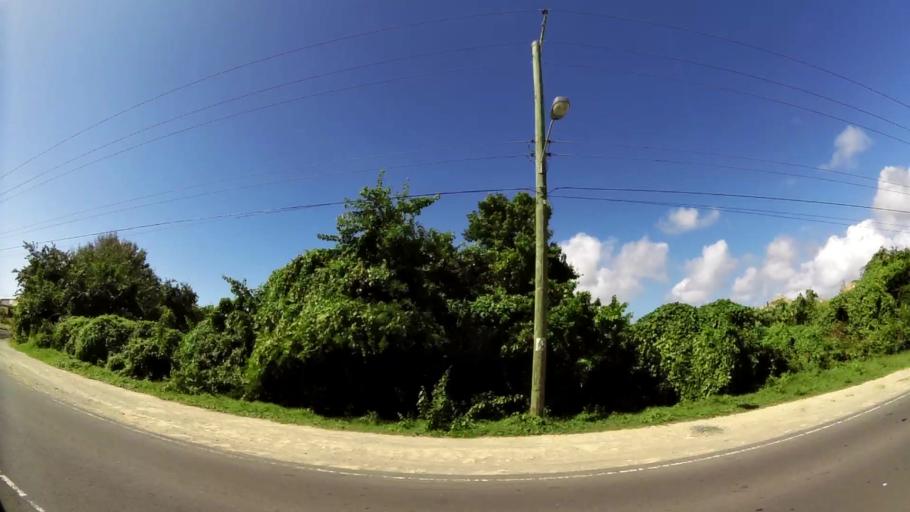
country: LC
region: Vieux-Fort
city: Vieux Fort
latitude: 13.7466
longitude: -60.9441
